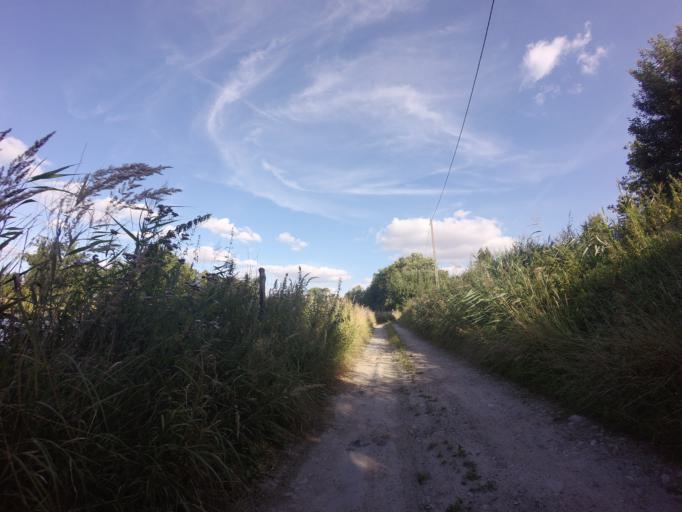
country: PL
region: West Pomeranian Voivodeship
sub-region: Powiat choszczenski
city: Choszczno
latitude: 53.1457
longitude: 15.4358
